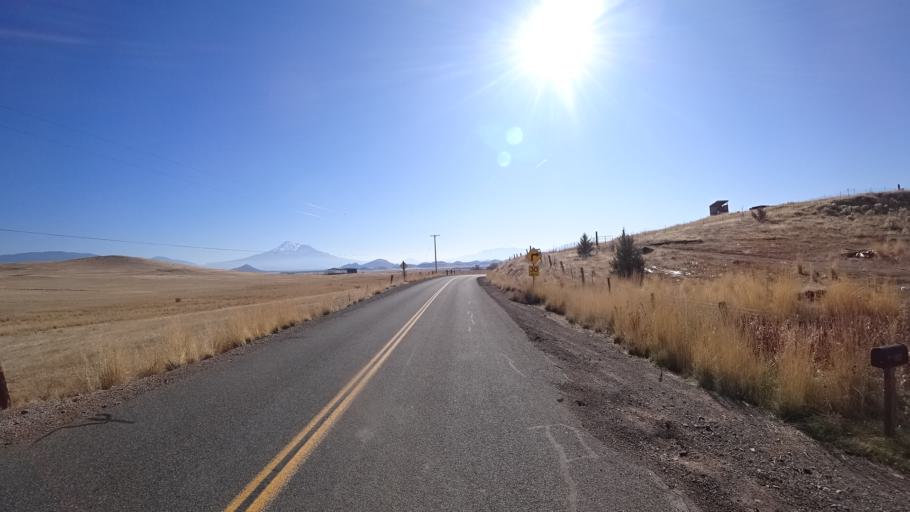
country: US
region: California
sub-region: Siskiyou County
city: Montague
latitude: 41.7407
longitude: -122.4568
